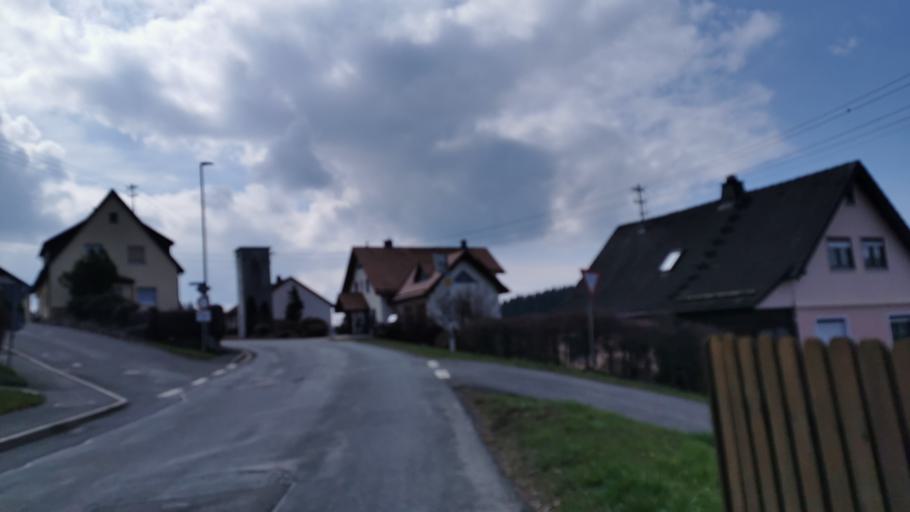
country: DE
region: Bavaria
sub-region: Upper Franconia
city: Tettau
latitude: 50.4215
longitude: 11.2907
